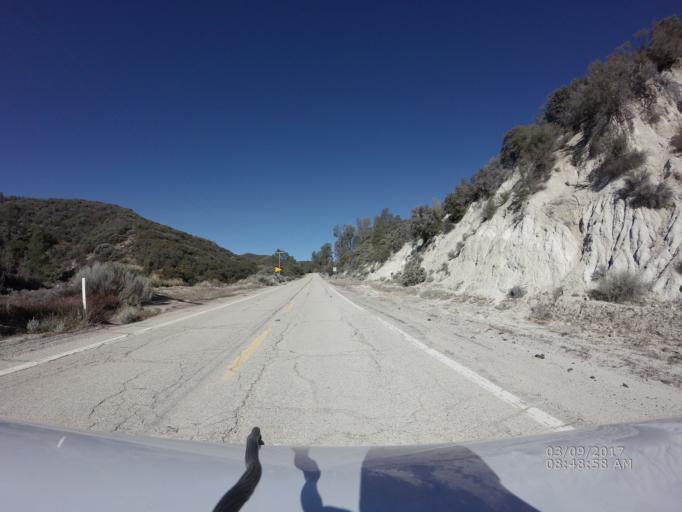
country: US
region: California
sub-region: Los Angeles County
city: Green Valley
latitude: 34.7020
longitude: -118.5235
